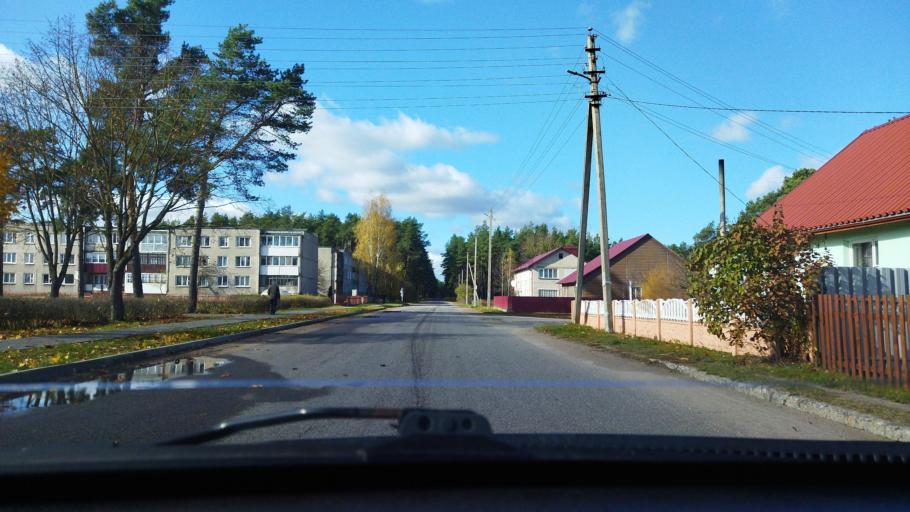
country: BY
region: Minsk
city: Svir
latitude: 54.8081
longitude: 26.2301
